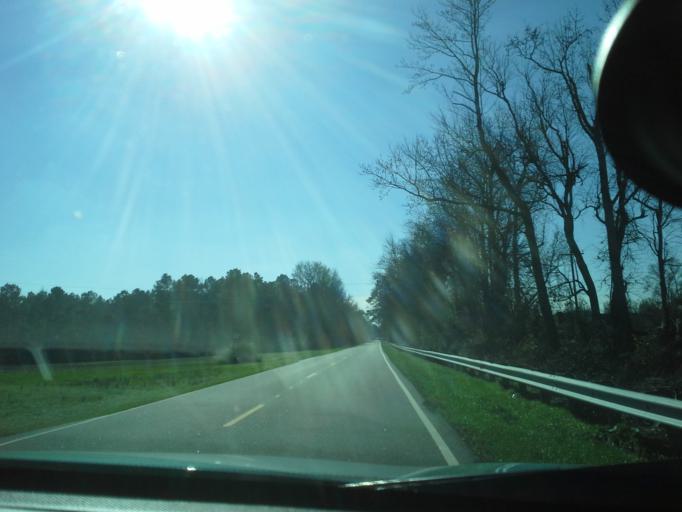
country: US
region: North Carolina
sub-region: Beaufort County
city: Belhaven
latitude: 35.6015
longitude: -76.6616
